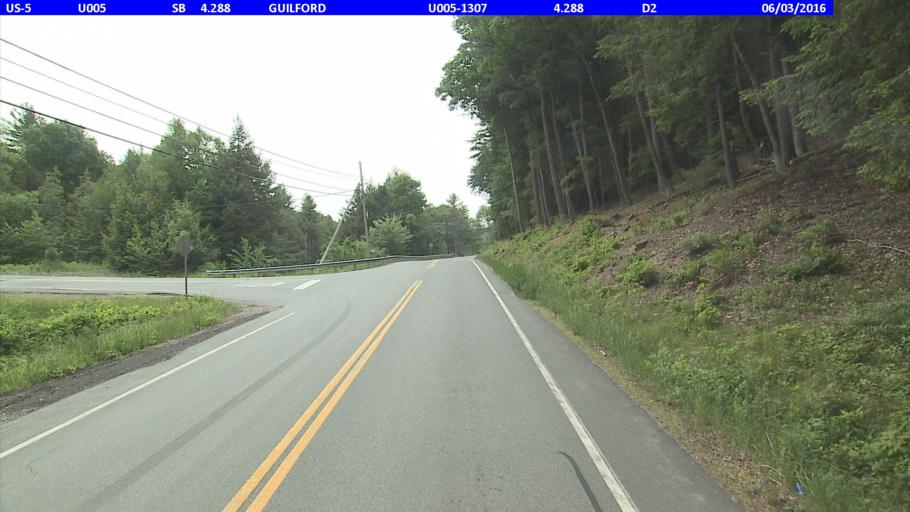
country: US
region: Vermont
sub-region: Windham County
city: Brattleboro
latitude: 42.7896
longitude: -72.5660
